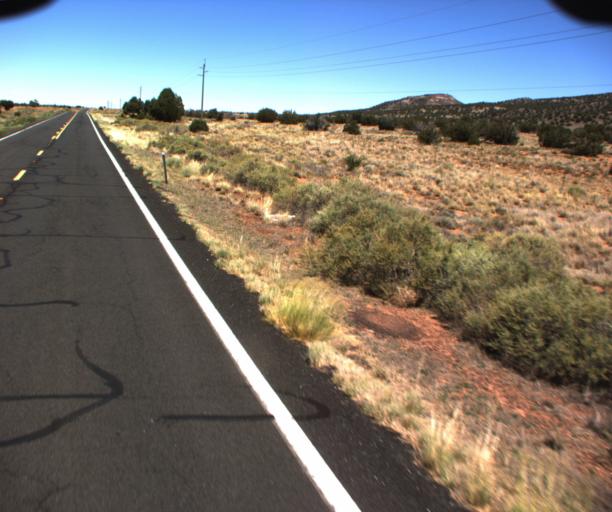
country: US
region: Arizona
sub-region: Coconino County
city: LeChee
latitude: 34.8559
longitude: -110.9210
